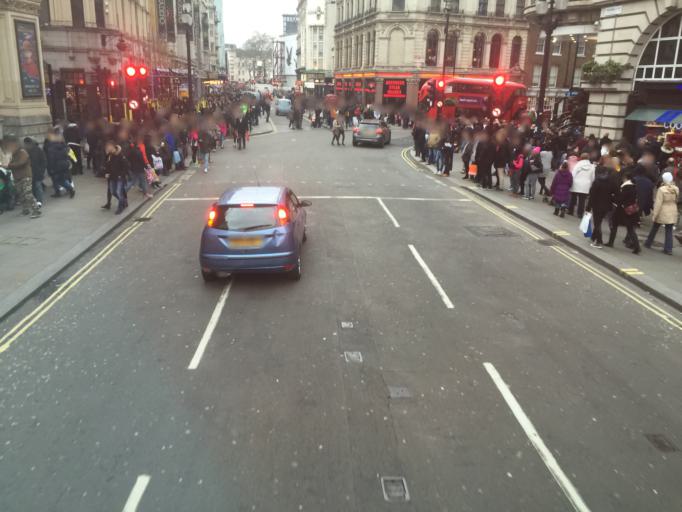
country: GB
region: England
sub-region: Greater London
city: London
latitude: 51.5100
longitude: -0.1339
